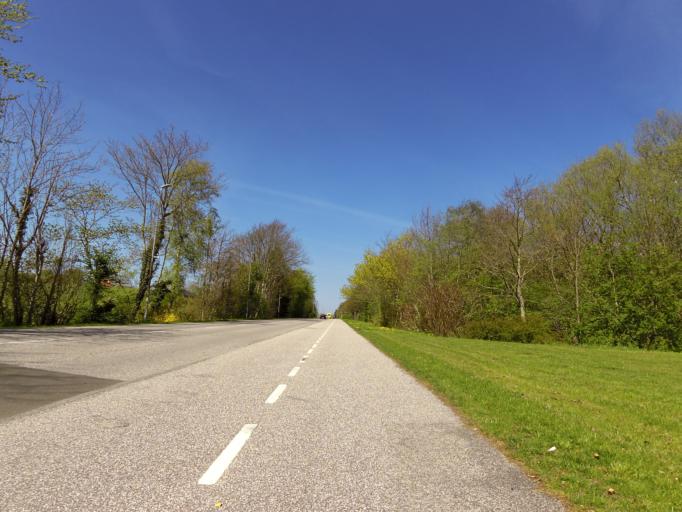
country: DK
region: Central Jutland
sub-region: Struer Kommune
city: Struer
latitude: 56.5057
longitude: 8.5803
